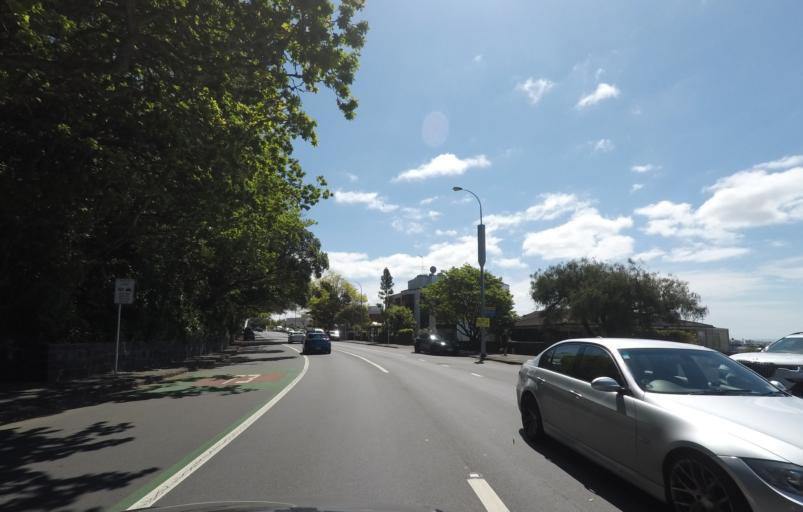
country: NZ
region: Auckland
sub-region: Auckland
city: Auckland
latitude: -36.8772
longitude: 174.7888
